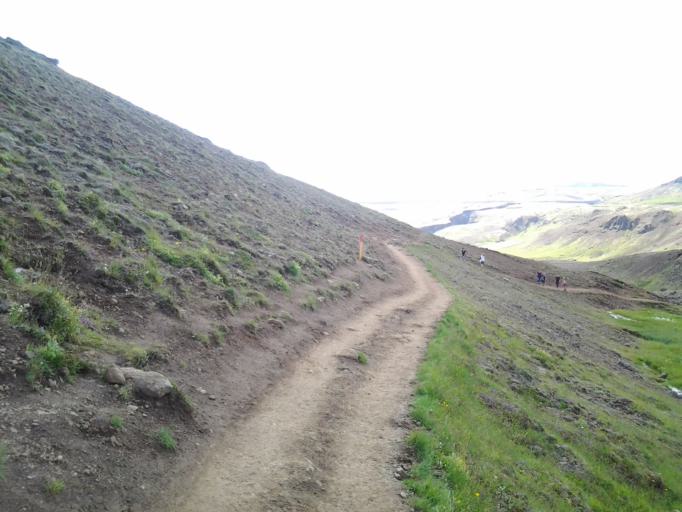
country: IS
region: South
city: Hveragerdi
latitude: 64.0293
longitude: -21.2150
